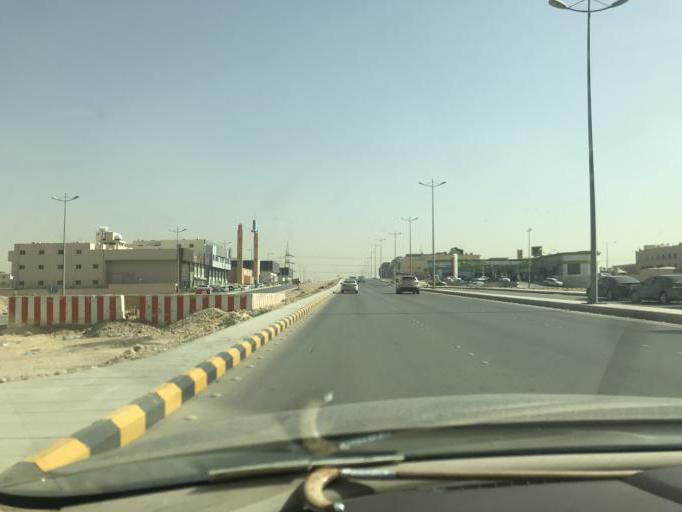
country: SA
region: Ar Riyad
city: Riyadh
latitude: 24.8221
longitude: 46.7290
